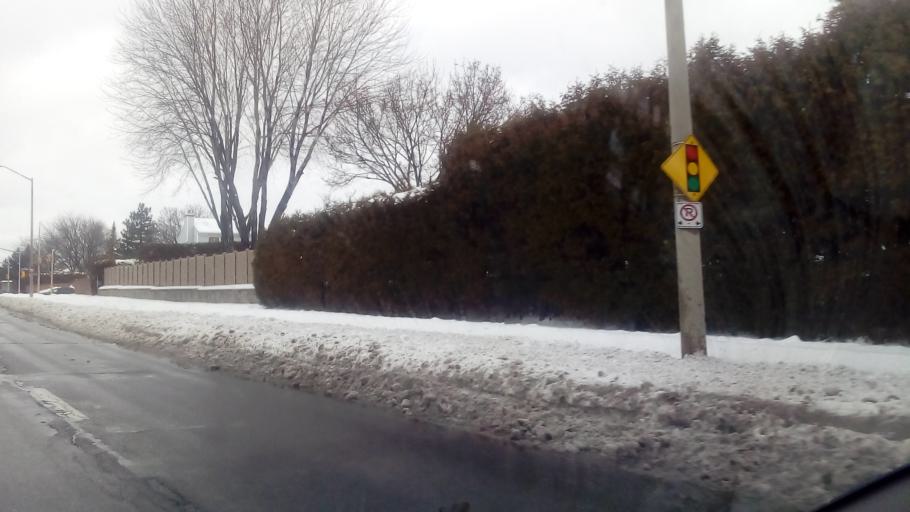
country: CA
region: Quebec
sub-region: Outaouais
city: Gatineau
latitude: 45.4594
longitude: -75.5193
